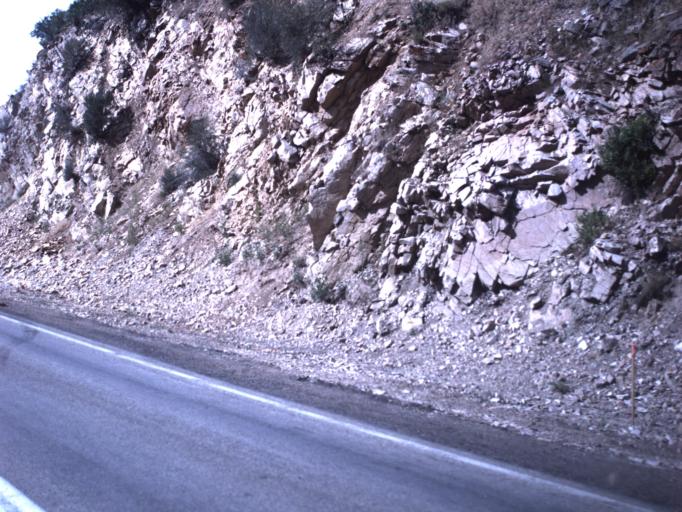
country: US
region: Utah
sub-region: Wasatch County
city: Heber
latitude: 40.3571
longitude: -111.2825
